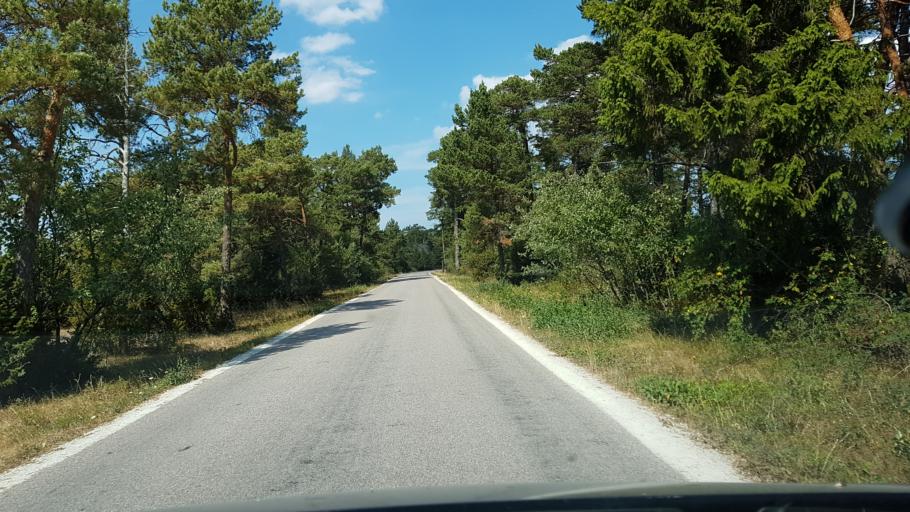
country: SE
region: Gotland
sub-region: Gotland
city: Visby
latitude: 57.6737
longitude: 18.3608
